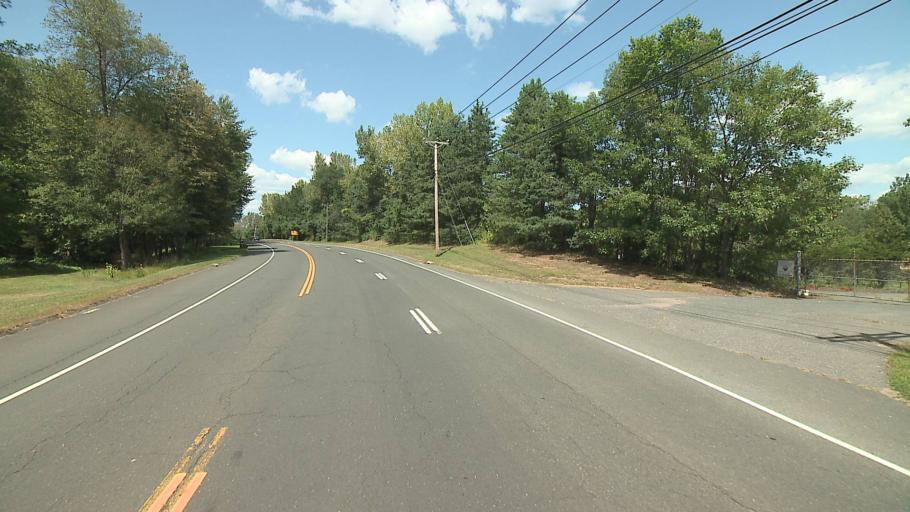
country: US
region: Connecticut
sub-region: Hartford County
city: Broad Brook
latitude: 41.9277
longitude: -72.5090
